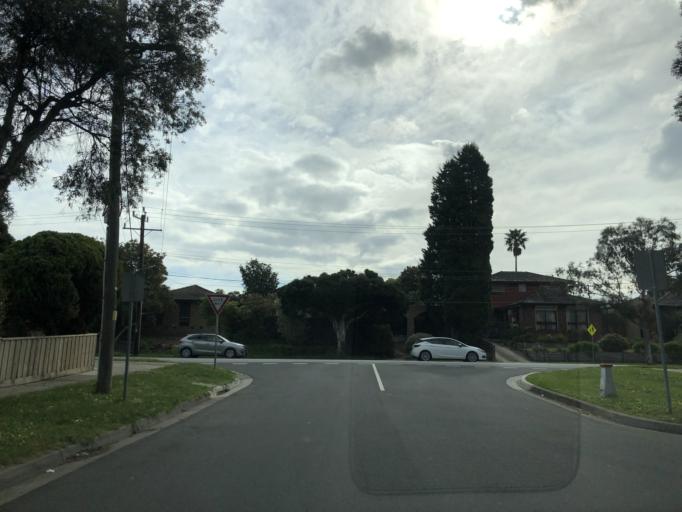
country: AU
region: Victoria
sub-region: Greater Dandenong
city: Noble Park North
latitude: -37.9495
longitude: 145.1928
